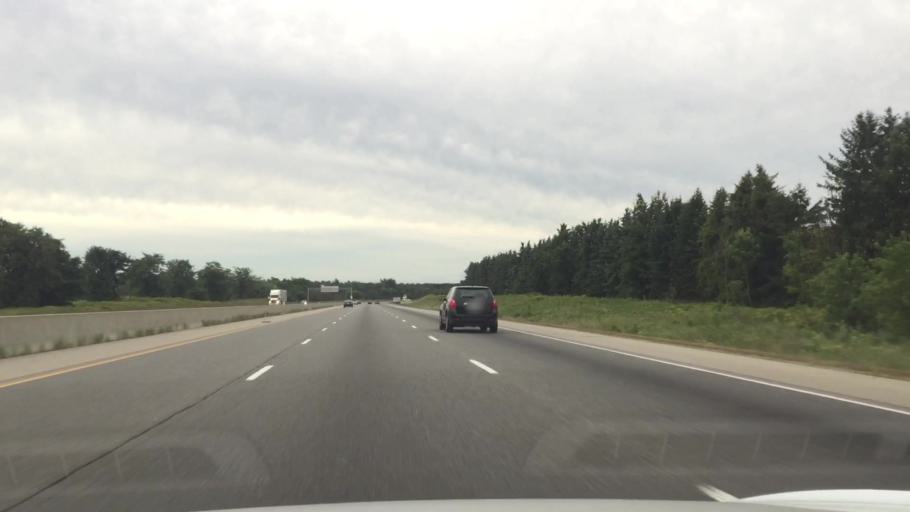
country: CA
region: Ontario
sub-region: Oxford County
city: Woodstock
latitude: 43.2205
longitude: -80.6047
